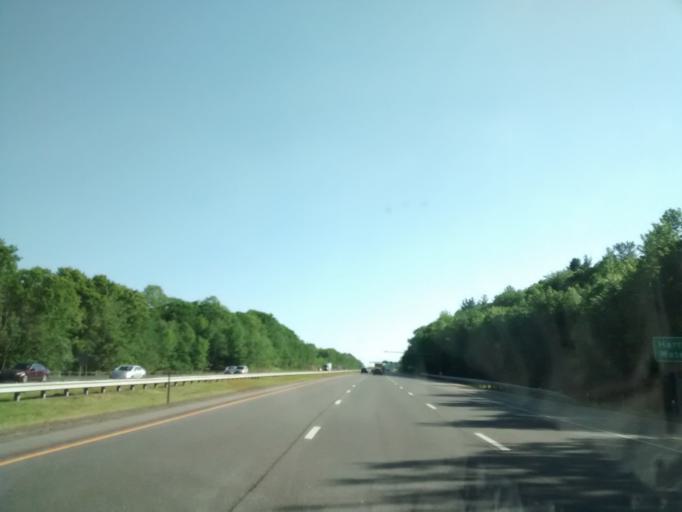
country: US
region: Massachusetts
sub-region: Hampden County
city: Holland
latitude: 41.9962
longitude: -72.1680
